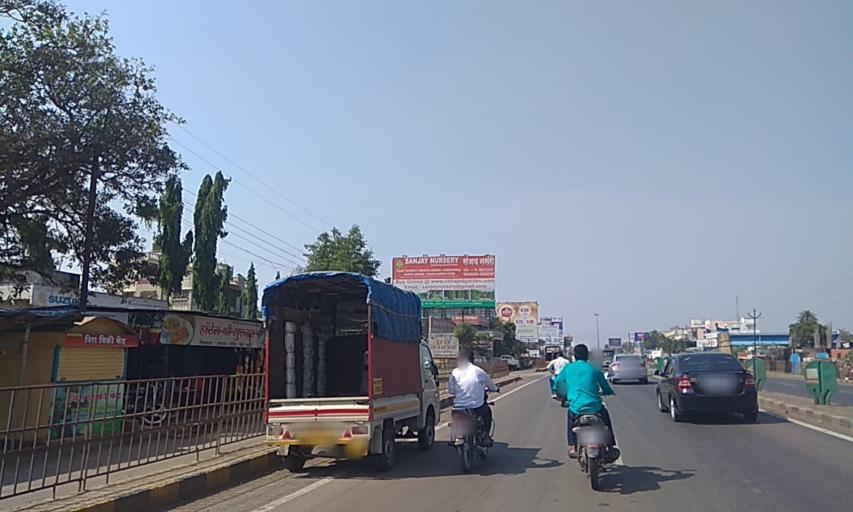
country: IN
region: Maharashtra
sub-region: Pune Division
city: Lohogaon
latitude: 18.4917
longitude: 74.0031
